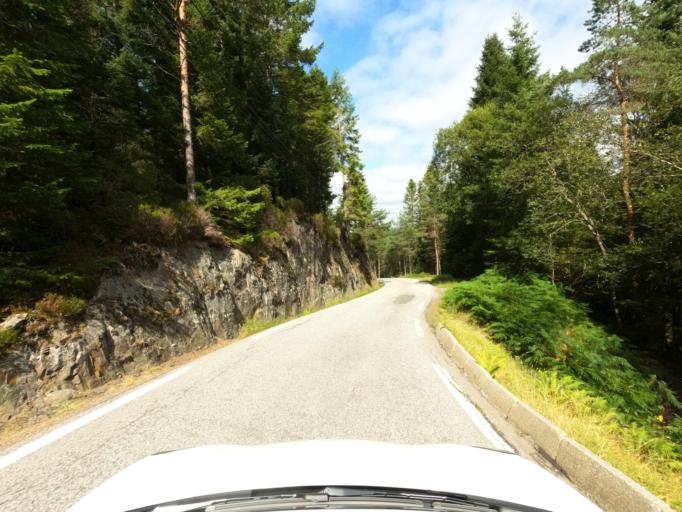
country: NO
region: Hordaland
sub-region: Os
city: Hagavik
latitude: 60.1732
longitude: 5.3597
